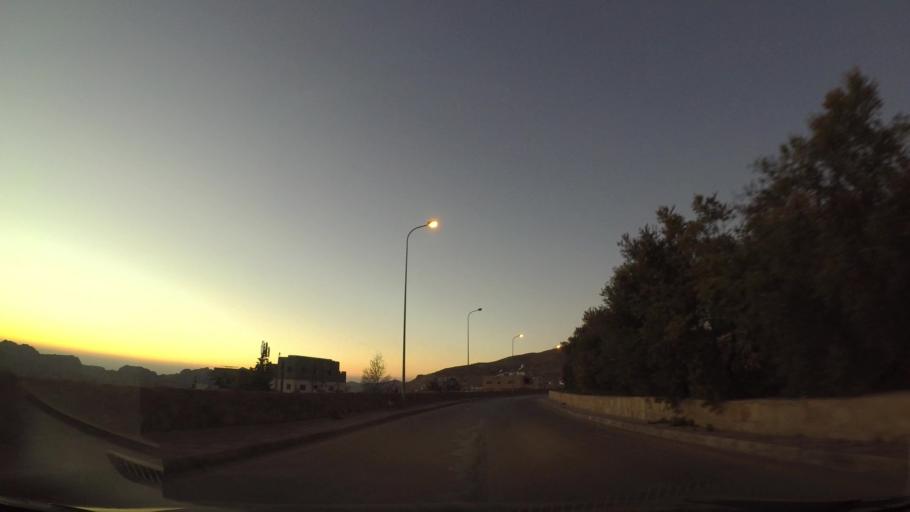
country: JO
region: Ma'an
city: Petra
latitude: 30.3221
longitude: 35.4814
